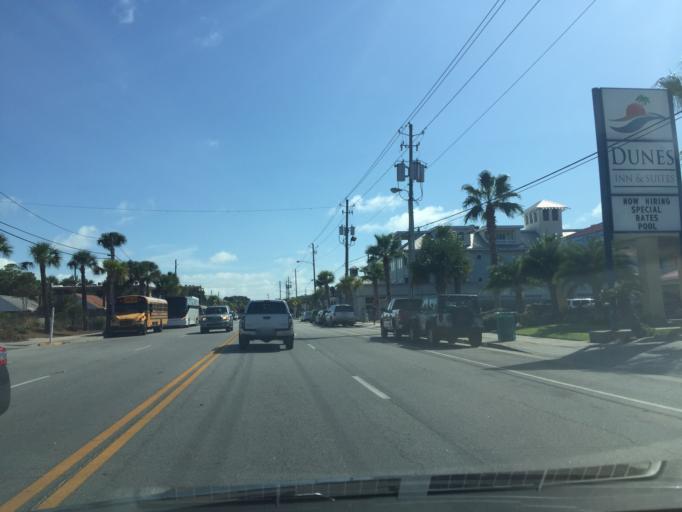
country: US
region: Georgia
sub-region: Chatham County
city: Tybee Island
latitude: 31.9953
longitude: -80.8482
